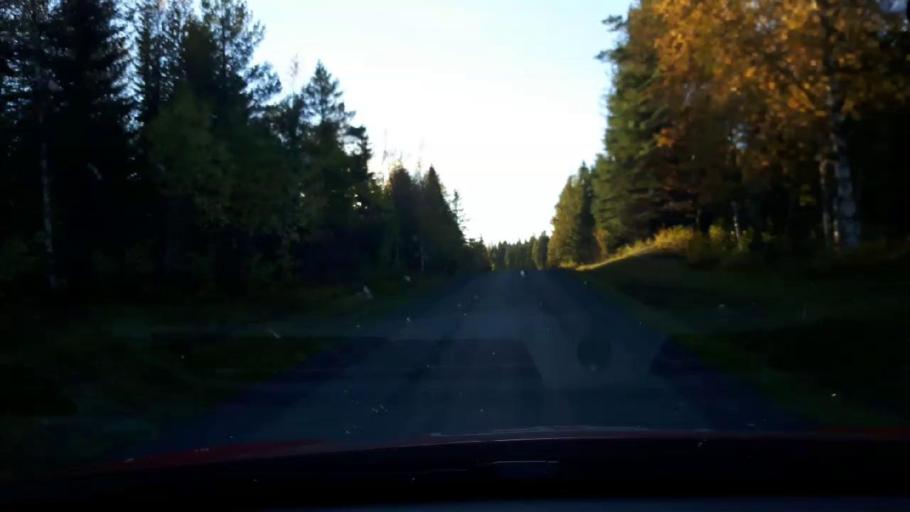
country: SE
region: Jaemtland
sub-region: OEstersunds Kommun
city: Lit
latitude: 63.4135
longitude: 14.6831
